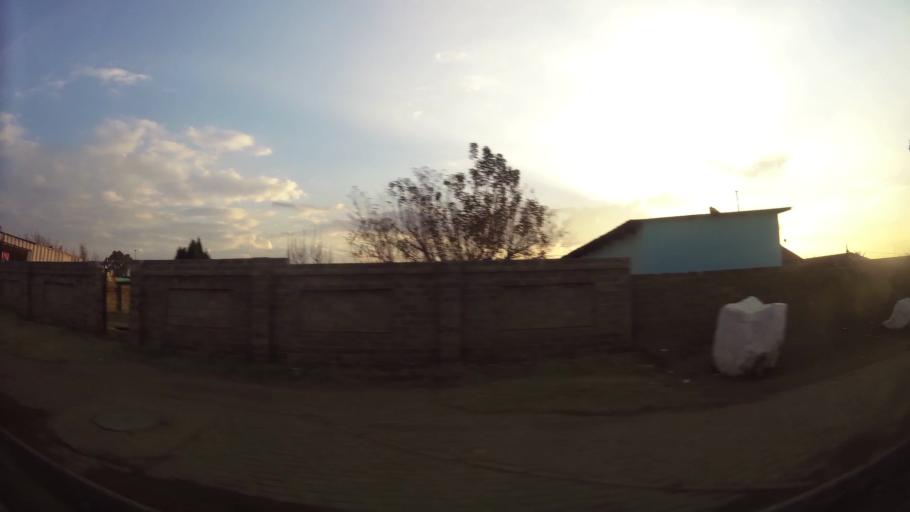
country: ZA
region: Gauteng
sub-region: City of Johannesburg Metropolitan Municipality
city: Orange Farm
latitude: -26.5403
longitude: 27.8840
